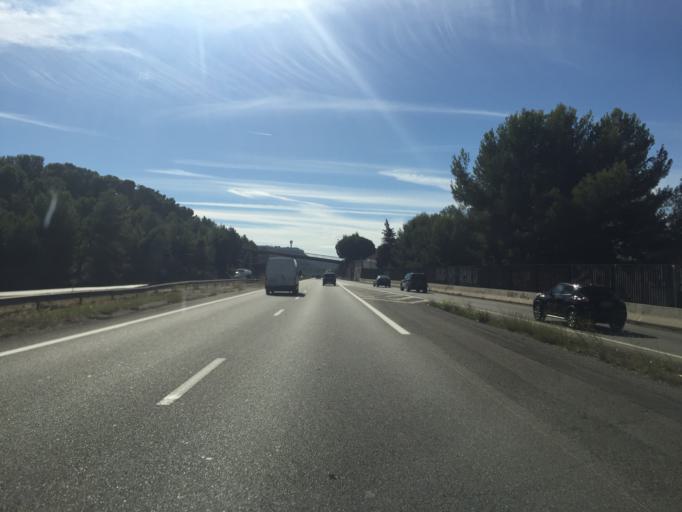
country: FR
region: Provence-Alpes-Cote d'Azur
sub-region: Departement des Bouches-du-Rhone
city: Rognac
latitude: 43.4935
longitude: 5.2396
